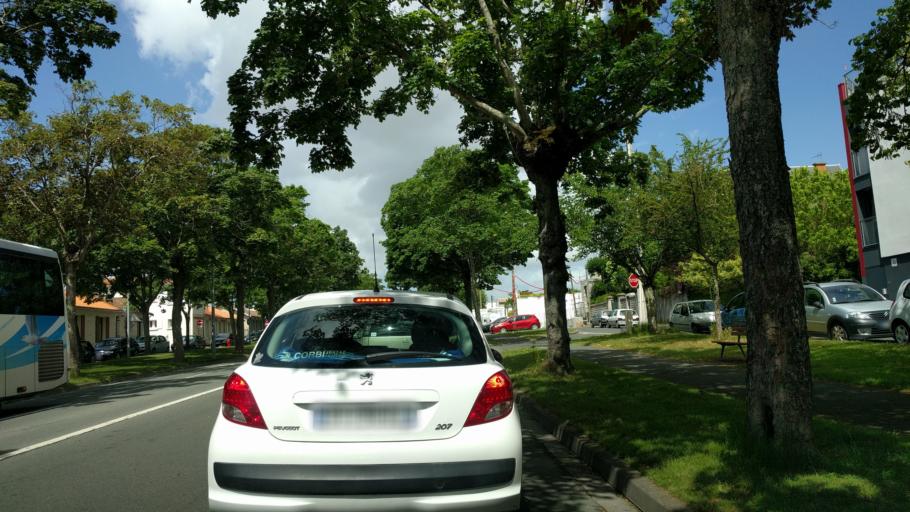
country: FR
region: Poitou-Charentes
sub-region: Departement de la Charente-Maritime
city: La Rochelle
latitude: 46.1669
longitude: -1.1379
